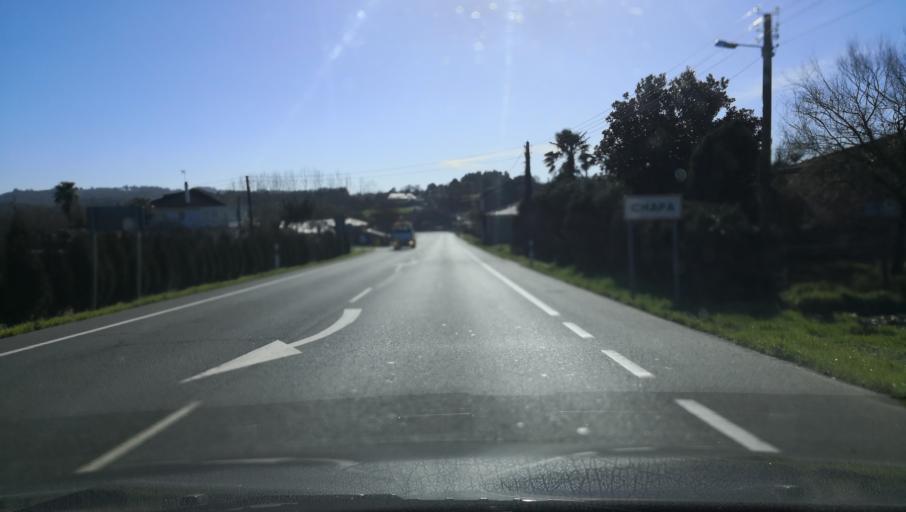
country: ES
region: Galicia
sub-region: Provincia de Pontevedra
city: Silleda
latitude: 42.7252
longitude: -8.2977
